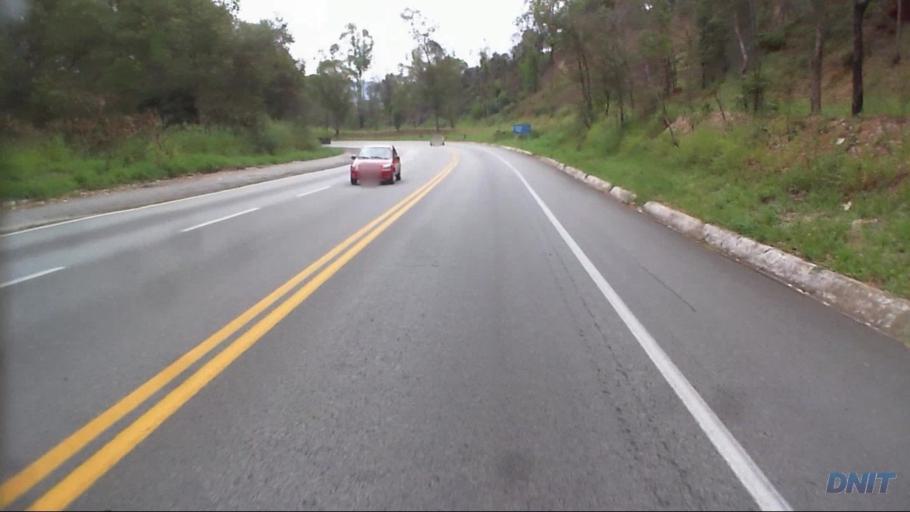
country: BR
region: Minas Gerais
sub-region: Joao Monlevade
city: Joao Monlevade
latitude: -19.8521
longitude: -43.1113
